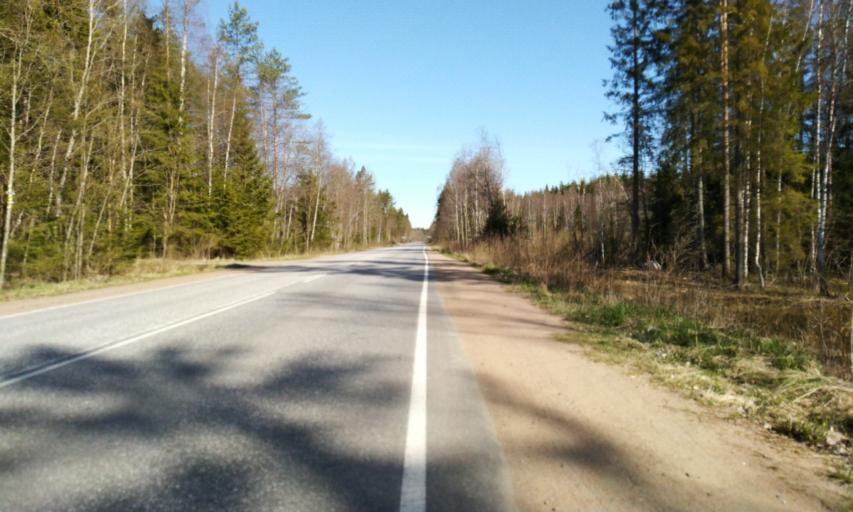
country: RU
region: Leningrad
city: Garbolovo
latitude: 60.3317
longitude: 30.4423
